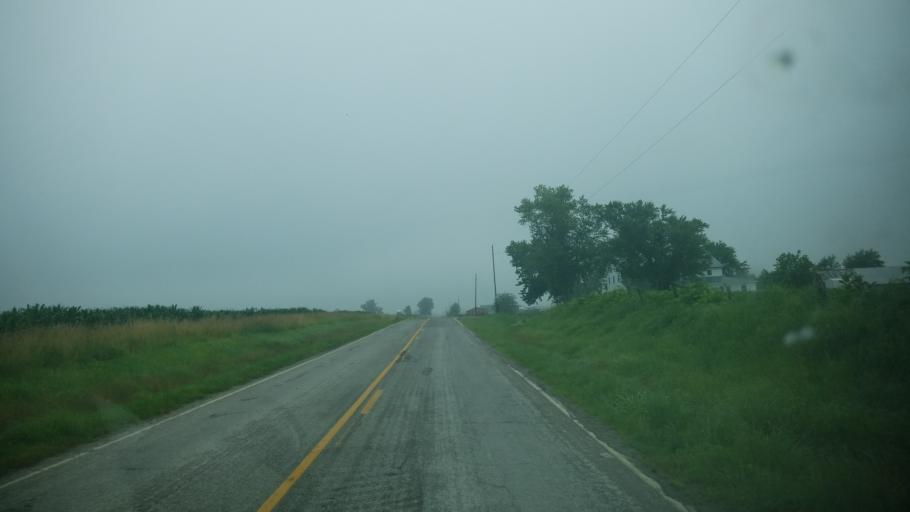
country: US
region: Missouri
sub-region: Audrain County
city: Vandalia
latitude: 39.3242
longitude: -91.3451
